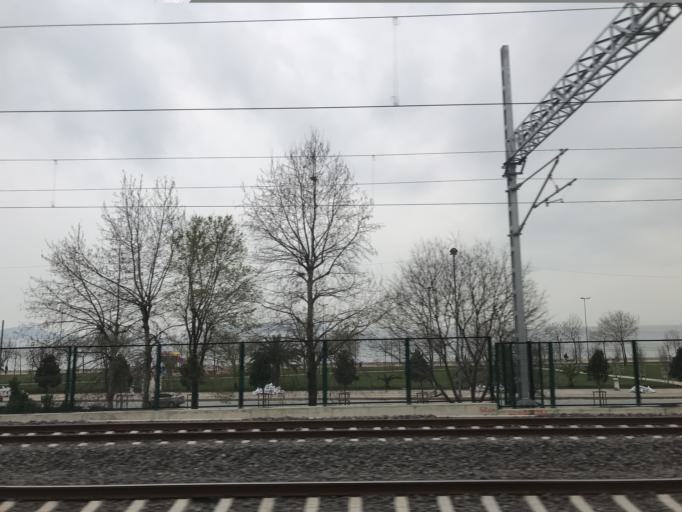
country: TR
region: Istanbul
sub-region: Atasehir
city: Atasehir
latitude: 40.9483
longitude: 29.1012
